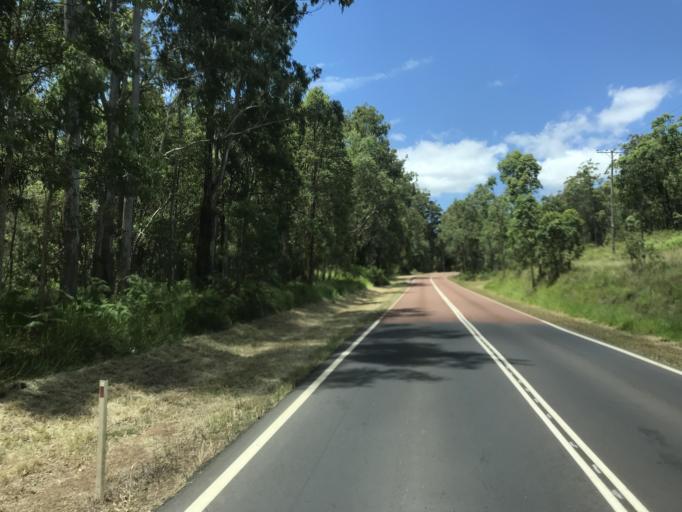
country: AU
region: Queensland
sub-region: Tablelands
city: Ravenshoe
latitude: -17.6014
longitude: 145.4781
